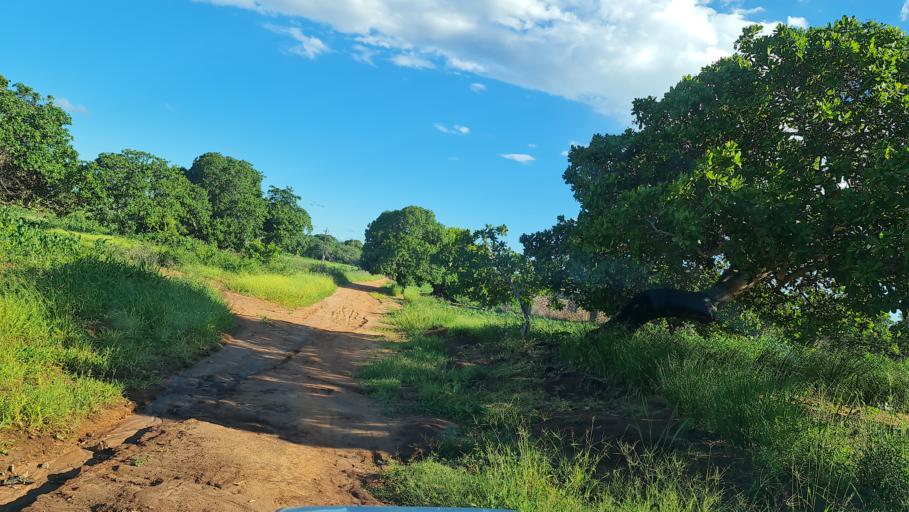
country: MZ
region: Nampula
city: Ilha de Mocambique
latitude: -14.9243
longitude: 40.2190
